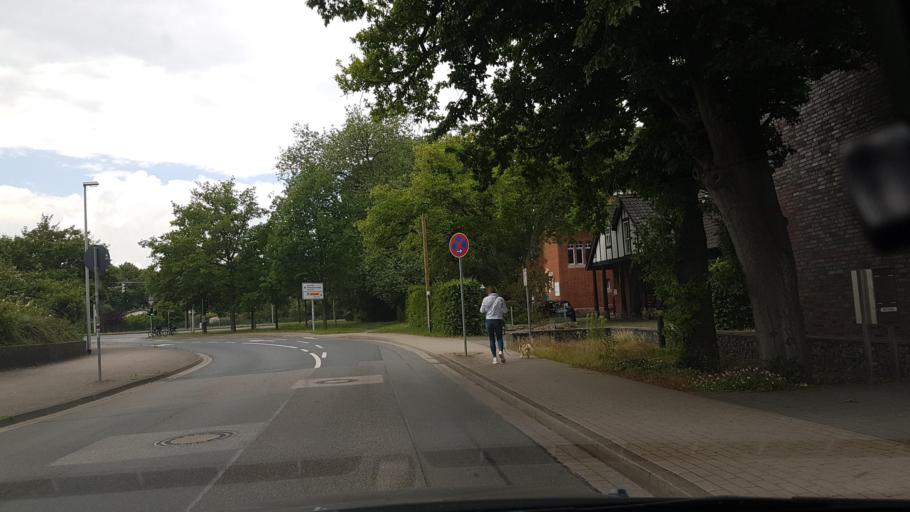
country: DE
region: Lower Saxony
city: Laatzen
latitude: 52.3549
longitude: 9.7976
